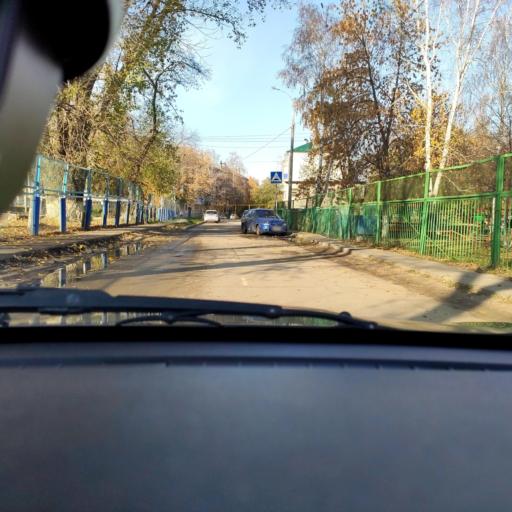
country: RU
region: Samara
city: Tol'yatti
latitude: 53.5272
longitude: 49.4012
